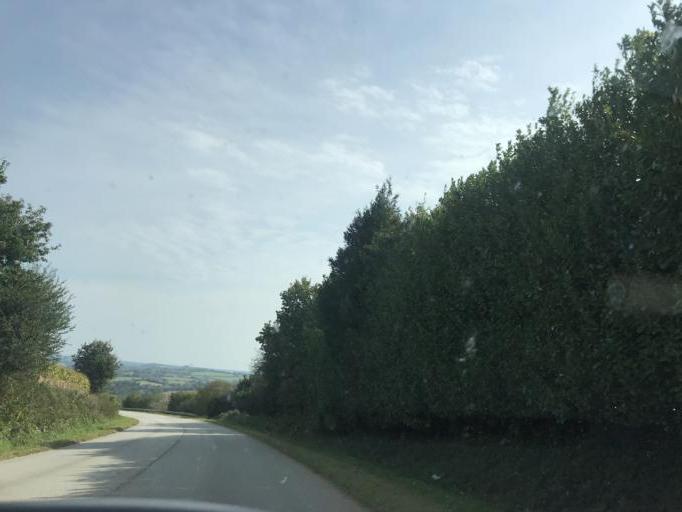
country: FR
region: Brittany
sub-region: Departement du Finistere
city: Loperec
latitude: 48.2925
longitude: -4.0510
